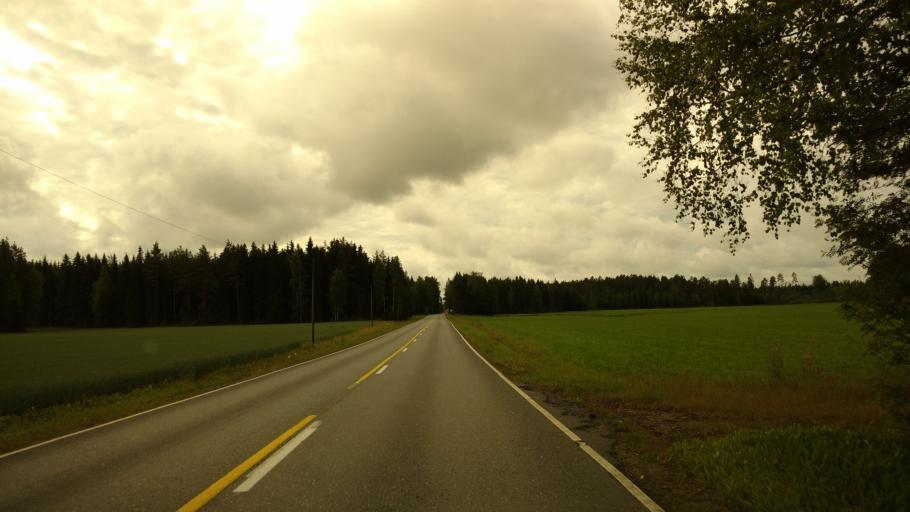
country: FI
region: Varsinais-Suomi
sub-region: Loimaa
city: Koski Tl
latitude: 60.5804
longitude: 23.1356
